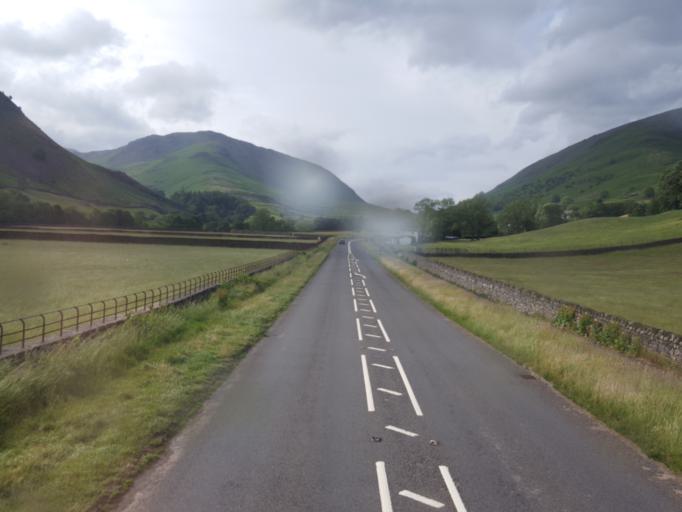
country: GB
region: England
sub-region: Cumbria
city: Ambleside
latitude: 54.4689
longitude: -3.0241
